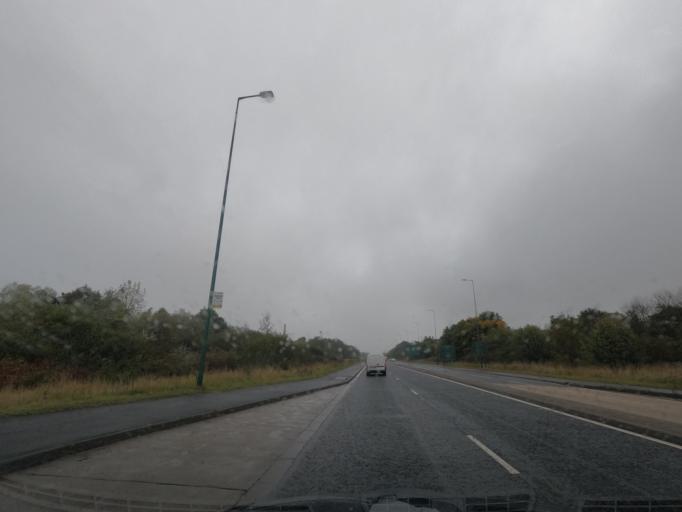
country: GB
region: England
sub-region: Redcar and Cleveland
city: South Bank
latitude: 54.5815
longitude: -1.1388
